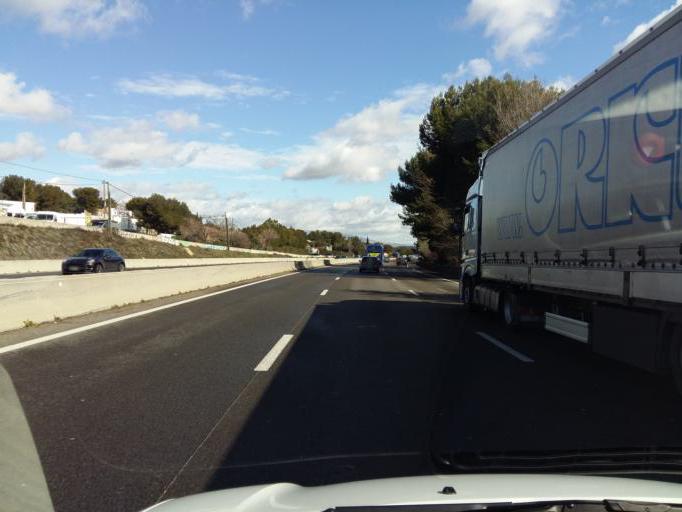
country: FR
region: Provence-Alpes-Cote d'Azur
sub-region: Departement des Bouches-du-Rhone
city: Cabries
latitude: 43.4254
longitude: 5.3774
